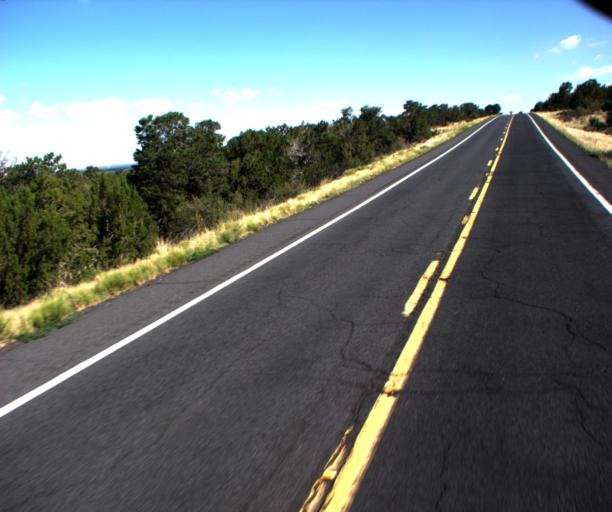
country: US
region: Arizona
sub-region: Coconino County
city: Williams
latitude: 35.4097
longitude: -112.1699
